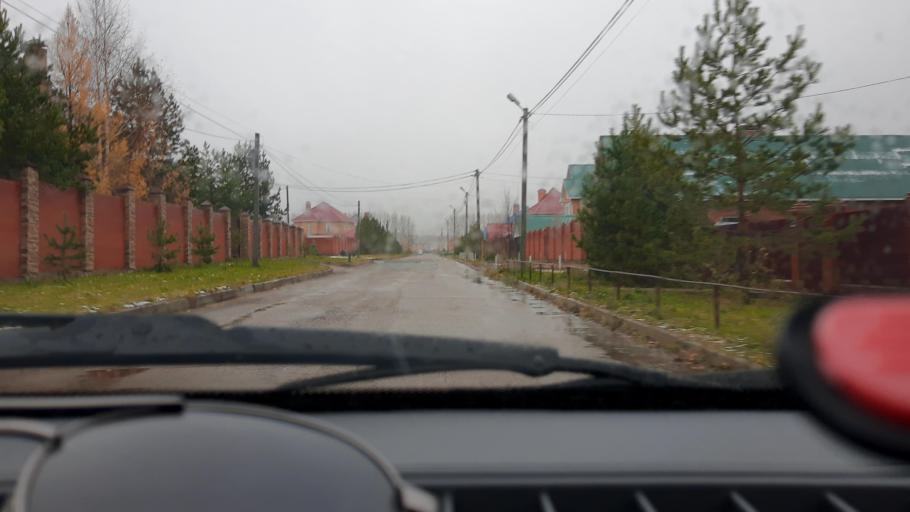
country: RU
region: Bashkortostan
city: Kabakovo
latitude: 54.6224
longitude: 56.1232
